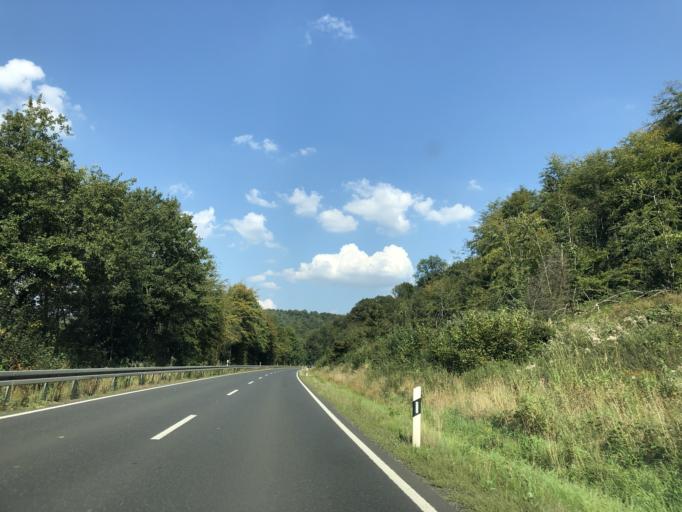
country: DE
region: Hesse
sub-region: Regierungsbezirk Giessen
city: Kirchhain
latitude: 50.8490
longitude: 8.9304
